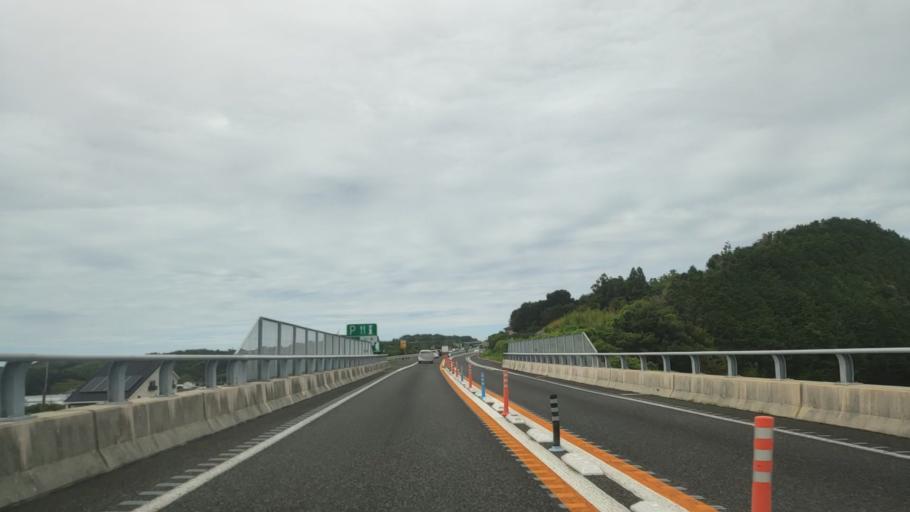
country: JP
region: Wakayama
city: Gobo
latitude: 33.8067
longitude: 135.2486
